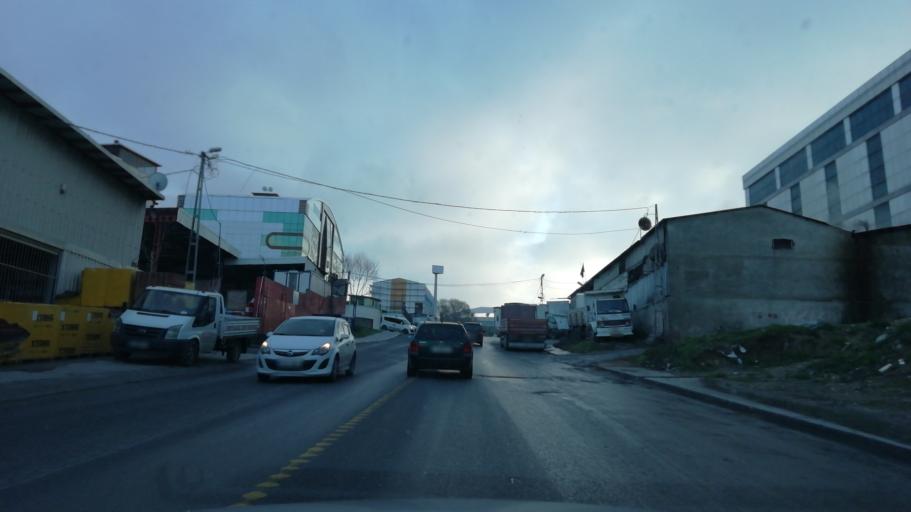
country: TR
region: Istanbul
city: Esenyurt
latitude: 41.0180
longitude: 28.7008
